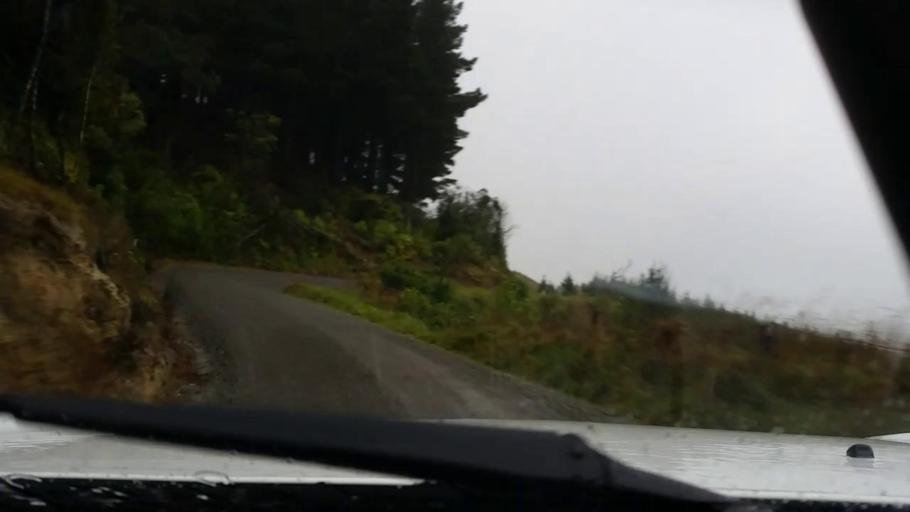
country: NZ
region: Wellington
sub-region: Masterton District
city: Masterton
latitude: -41.1921
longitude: 175.8136
